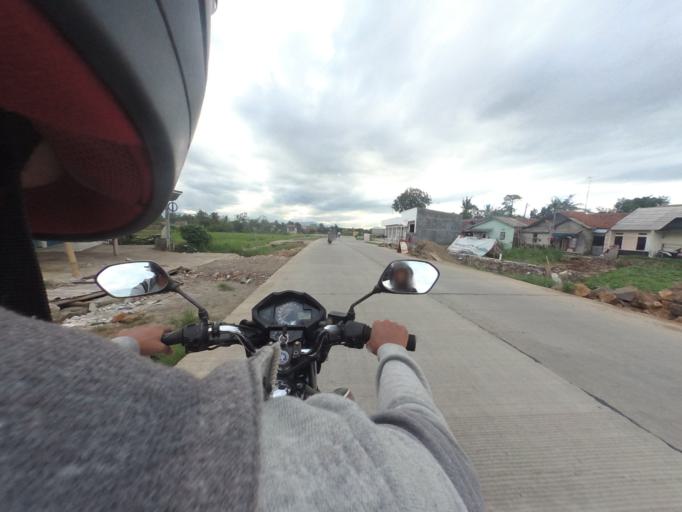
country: ID
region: West Java
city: Ciampea
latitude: -6.5789
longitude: 106.7421
